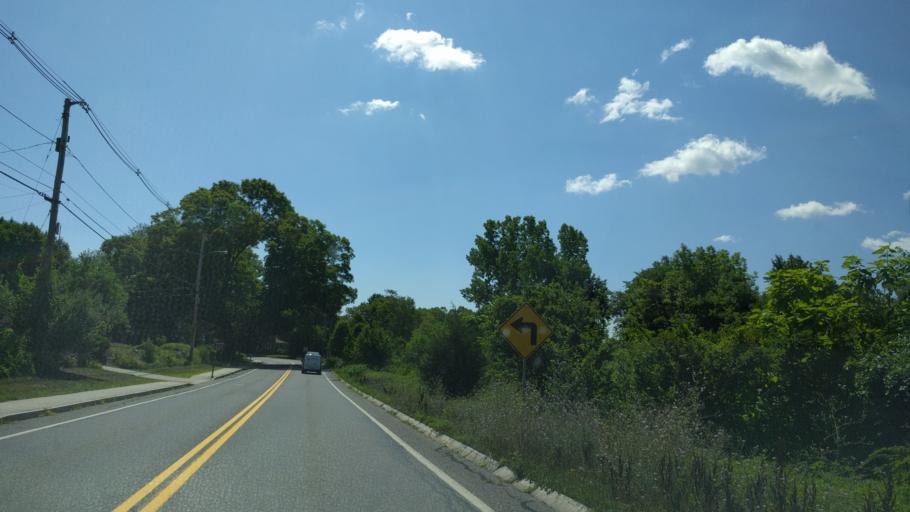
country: US
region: Massachusetts
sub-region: Middlesex County
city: Marlborough
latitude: 42.3324
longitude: -71.5363
